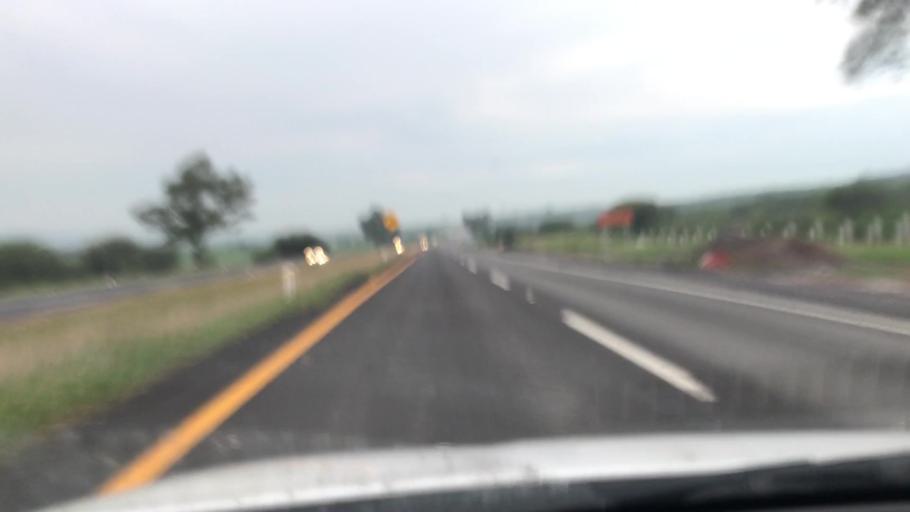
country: MX
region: Jalisco
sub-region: Zapotlanejo
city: La Mezquitera
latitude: 20.5678
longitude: -103.0797
